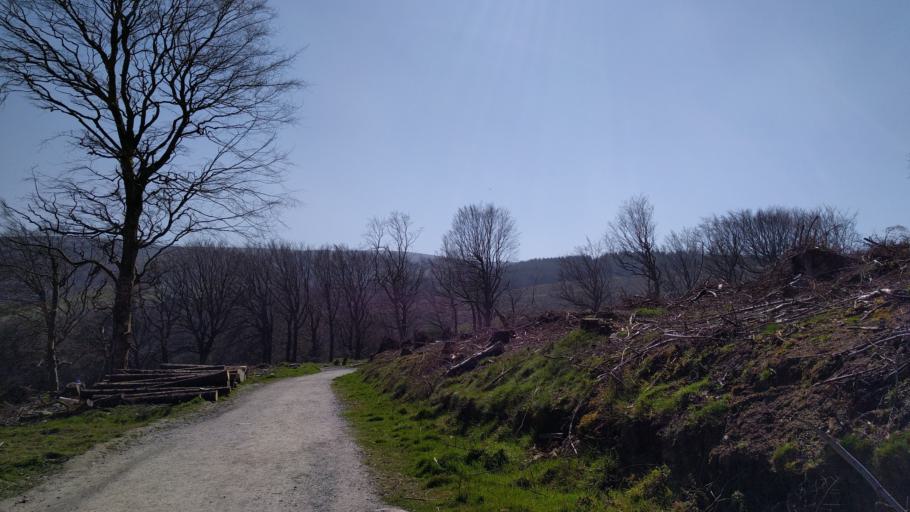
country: IE
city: Knocklyon
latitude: 53.2508
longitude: -6.3243
